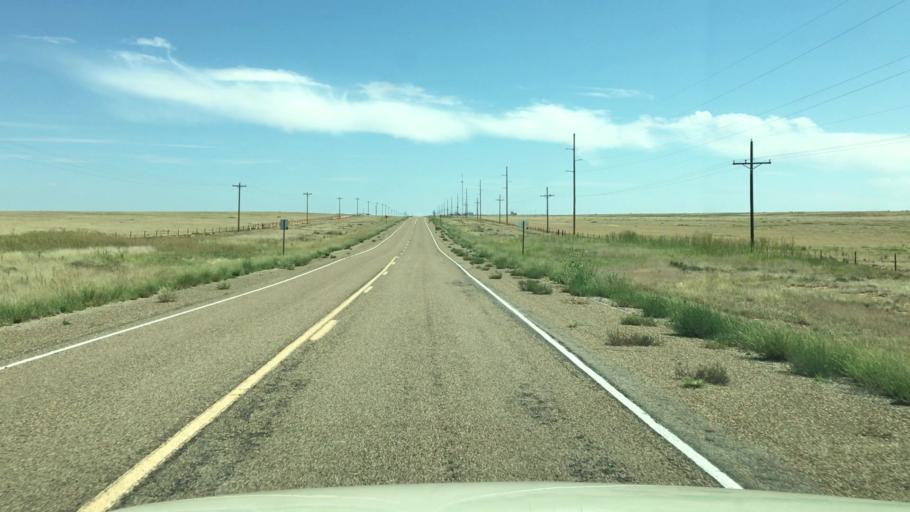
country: US
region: New Mexico
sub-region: Chaves County
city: Roswell
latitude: 33.9485
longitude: -104.5891
